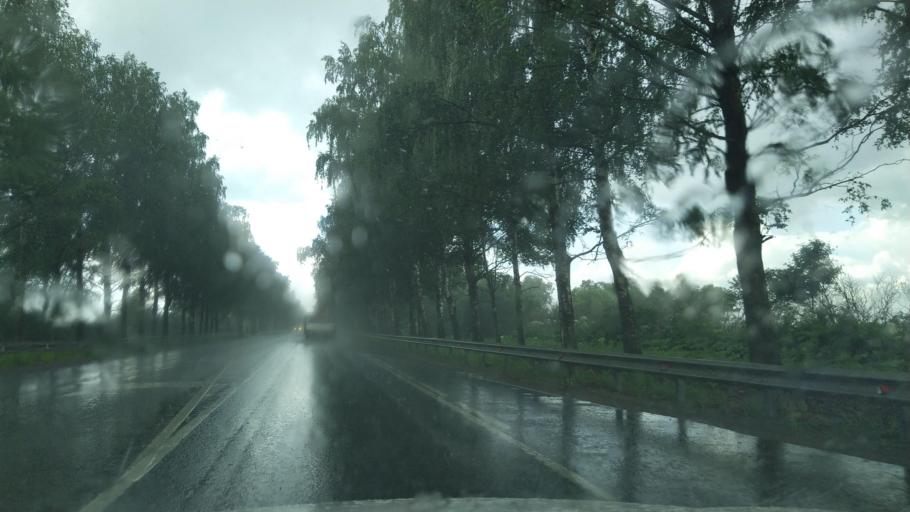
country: RU
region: Leningrad
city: Voyskovitsy
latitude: 59.4864
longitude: 30.0275
